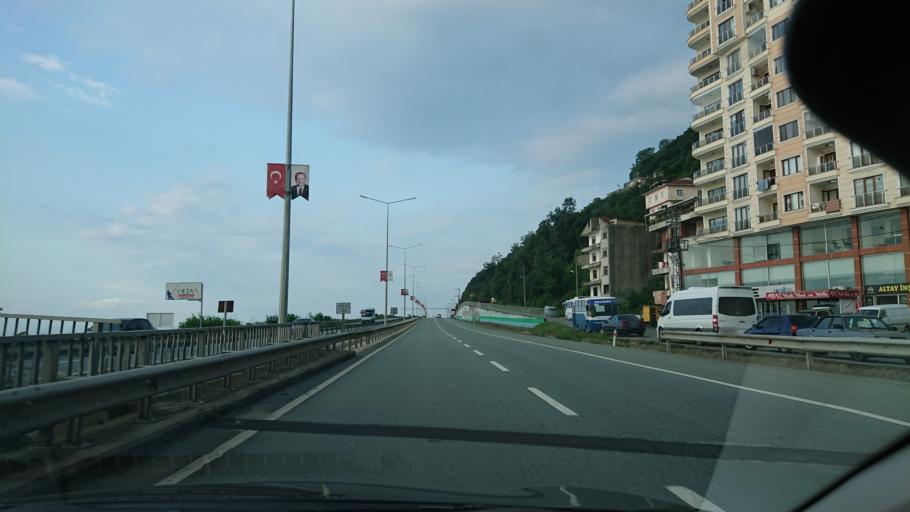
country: TR
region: Rize
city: Gundogdu
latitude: 41.0544
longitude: 40.6177
